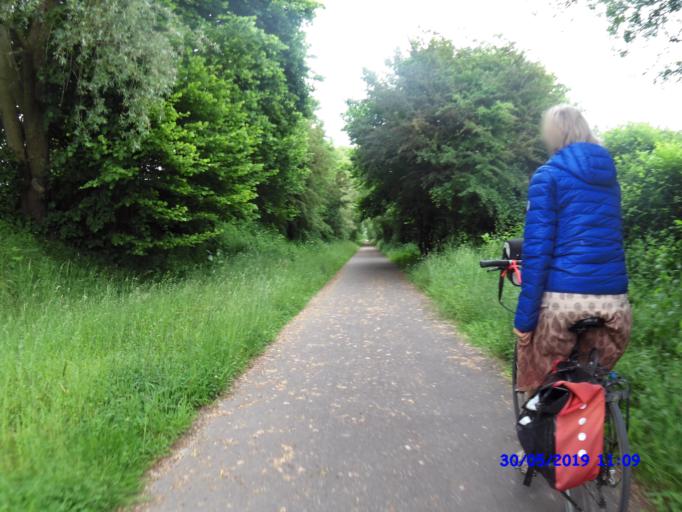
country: BE
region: Wallonia
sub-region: Province du Hainaut
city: Thuin
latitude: 50.2924
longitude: 4.3326
